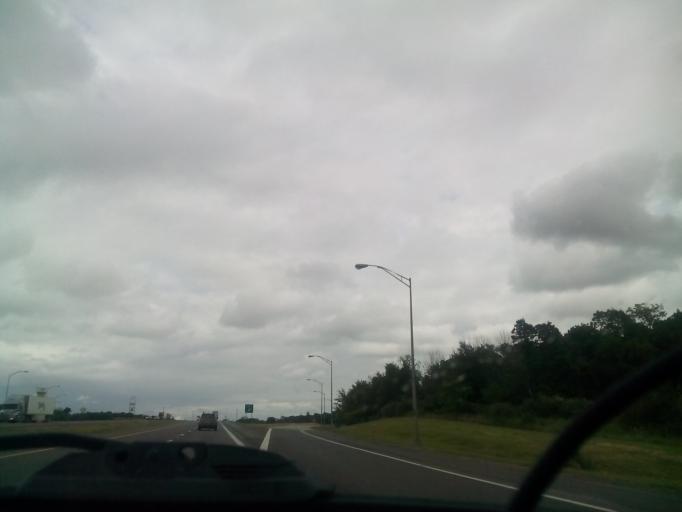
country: US
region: Indiana
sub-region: Steuben County
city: Hamilton
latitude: 41.6299
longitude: -84.7719
